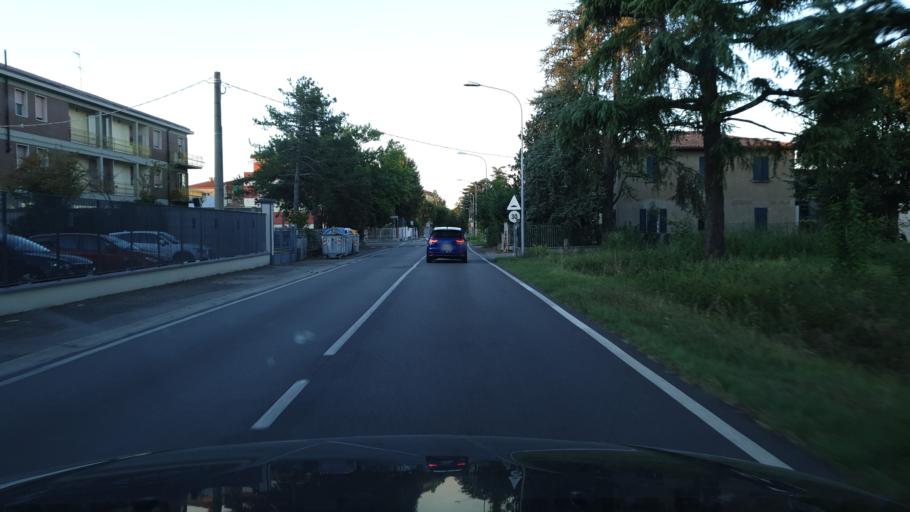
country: IT
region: Emilia-Romagna
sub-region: Provincia di Bologna
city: Quarto Inferiore
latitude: 44.5466
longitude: 11.3976
